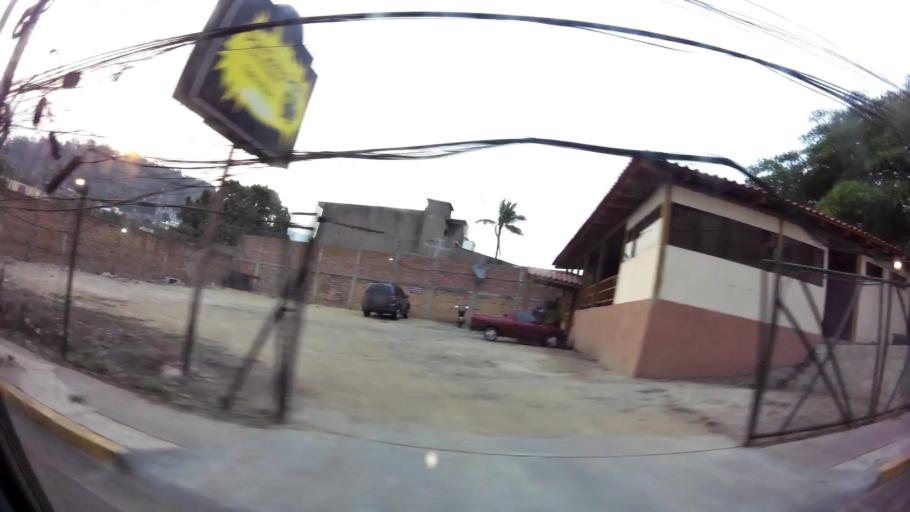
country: HN
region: Francisco Morazan
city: Tegucigalpa
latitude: 14.0913
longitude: -87.1946
